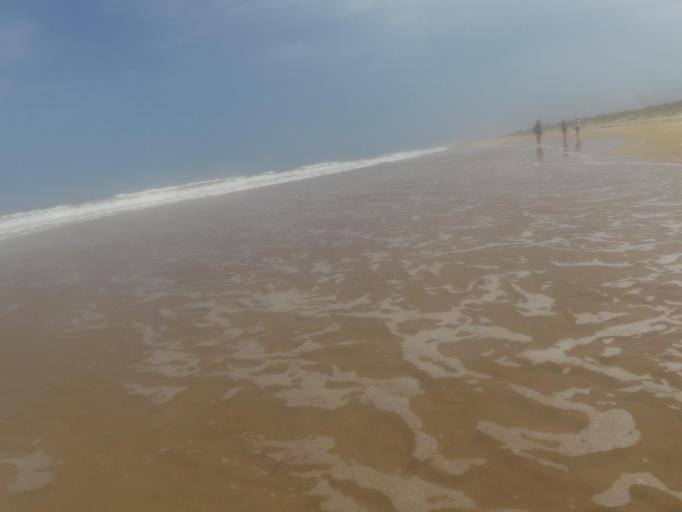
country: US
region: Florida
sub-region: Saint Johns County
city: Saint Augustine Beach
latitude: 29.8788
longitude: -81.2710
